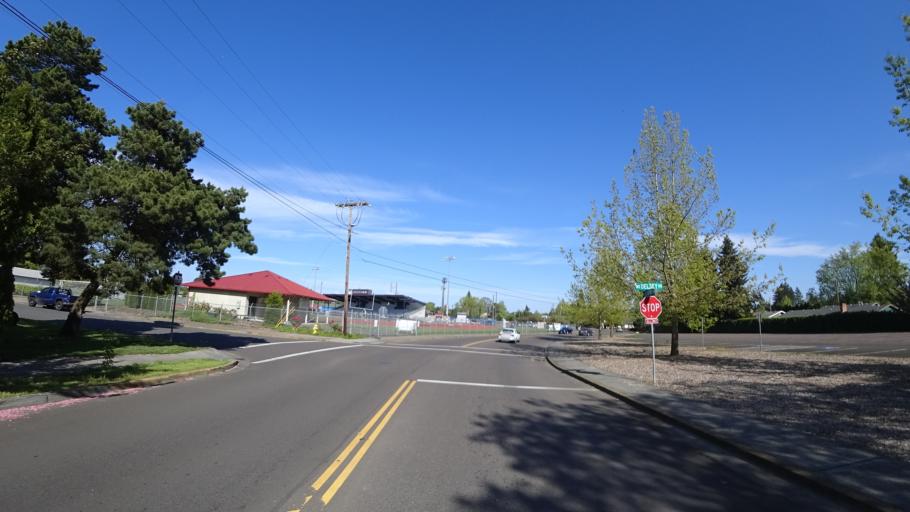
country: US
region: Oregon
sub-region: Washington County
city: Hillsboro
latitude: 45.5282
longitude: -122.9751
